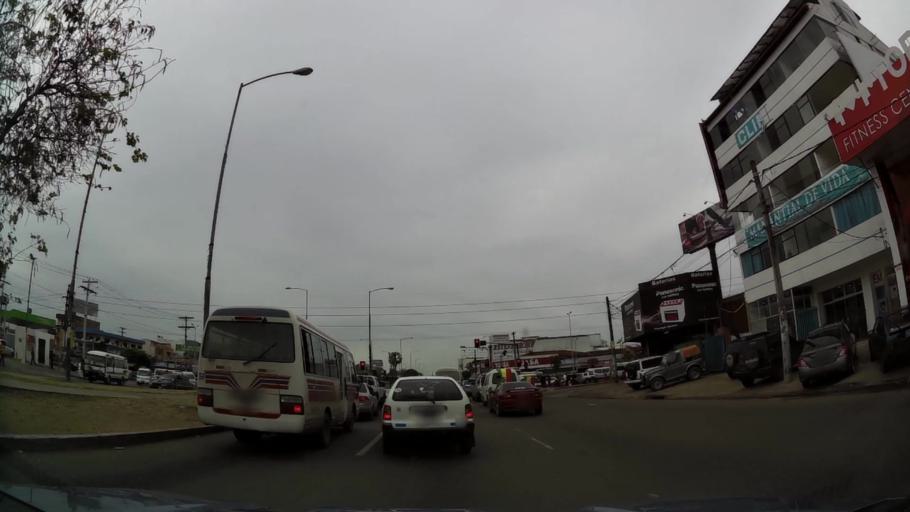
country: BO
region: Santa Cruz
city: Santa Cruz de la Sierra
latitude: -17.8043
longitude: -63.1997
